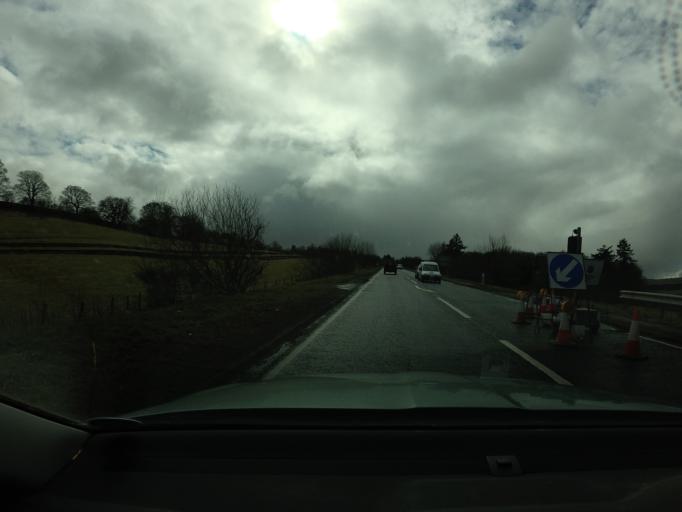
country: GB
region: Scotland
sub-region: South Lanarkshire
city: Douglas
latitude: 55.5736
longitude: -3.8168
